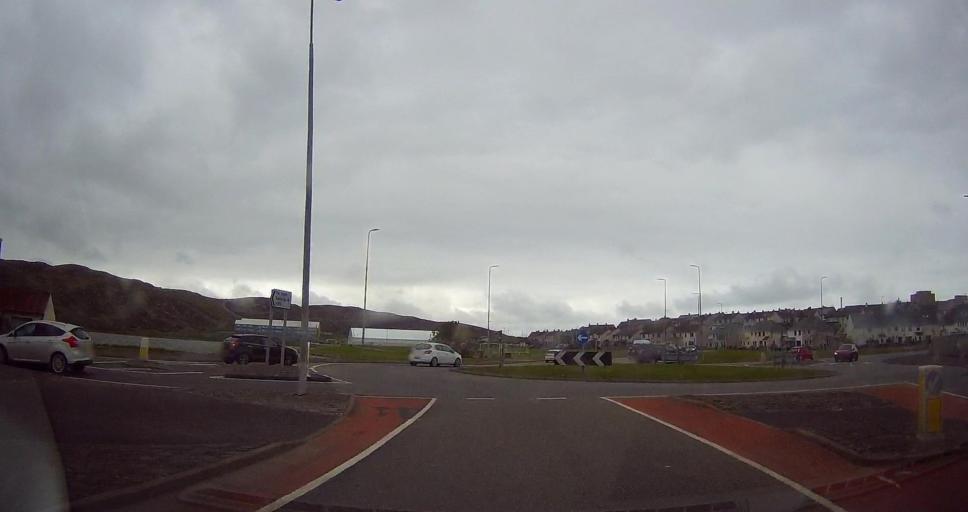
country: GB
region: Scotland
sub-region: Shetland Islands
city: Lerwick
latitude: 60.1485
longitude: -1.1626
